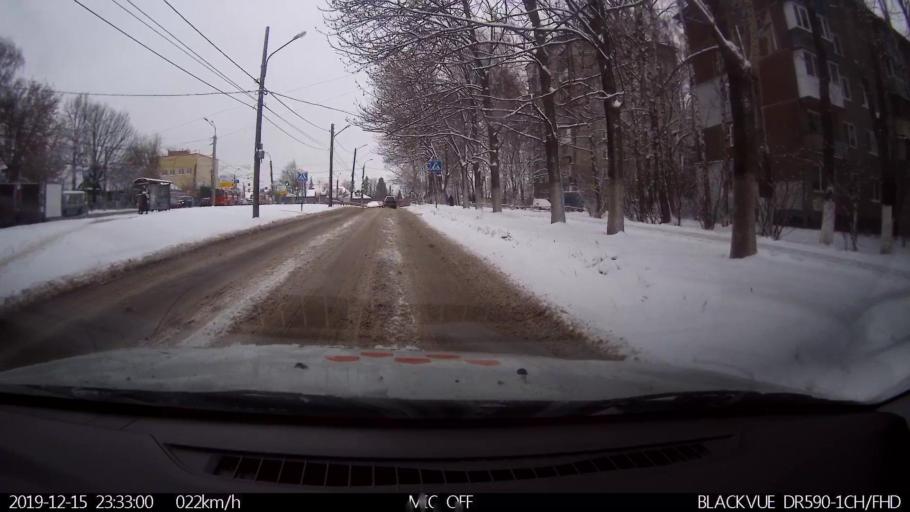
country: RU
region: Nizjnij Novgorod
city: Nizhniy Novgorod
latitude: 56.2990
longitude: 44.0333
